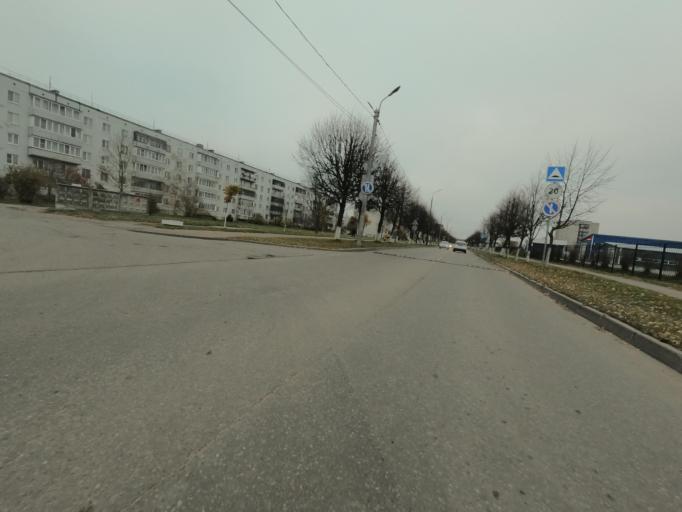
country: RU
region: Leningrad
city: Kirovsk
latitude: 59.8809
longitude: 30.9976
